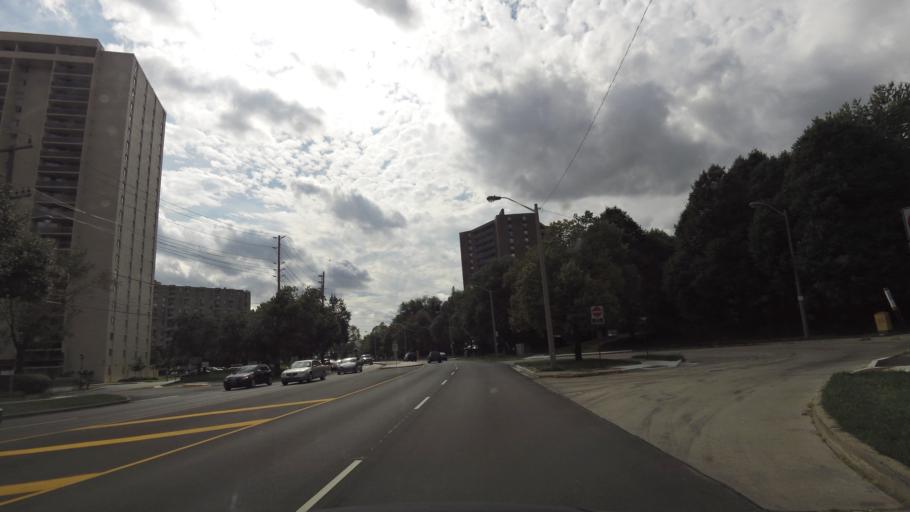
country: CA
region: Ontario
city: Etobicoke
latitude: 43.6406
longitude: -79.5824
